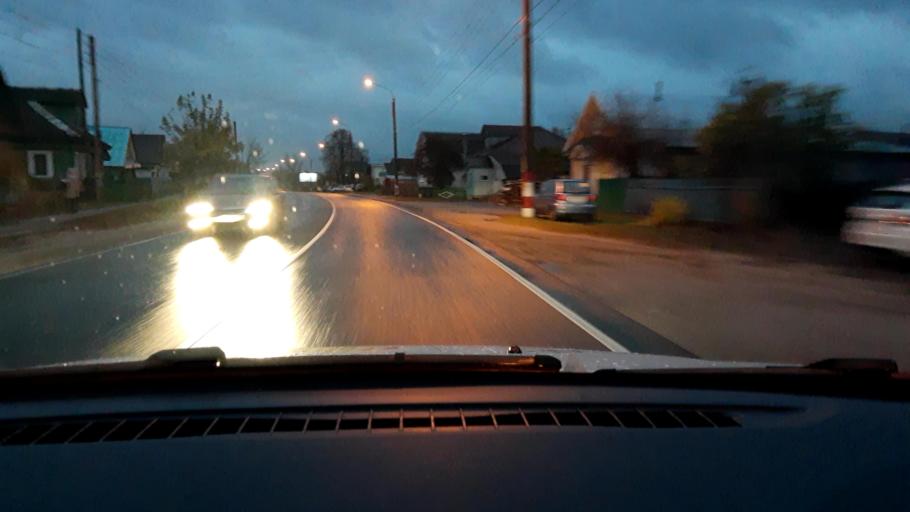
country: RU
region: Nizjnij Novgorod
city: Neklyudovo
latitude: 56.3805
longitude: 44.0154
